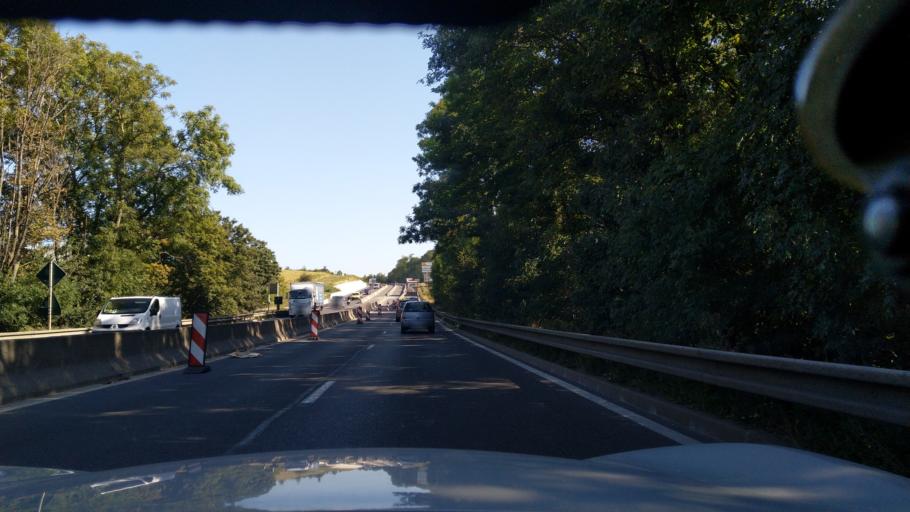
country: FR
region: Ile-de-France
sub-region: Departement du Val-d'Oise
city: Le Thillay
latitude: 49.0006
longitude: 2.4850
